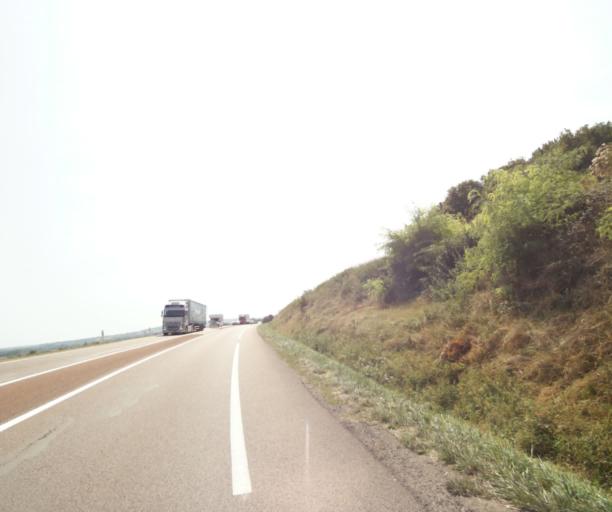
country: FR
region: Bourgogne
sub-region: Departement de Saone-et-Loire
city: Tournus
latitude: 46.5939
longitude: 4.9061
